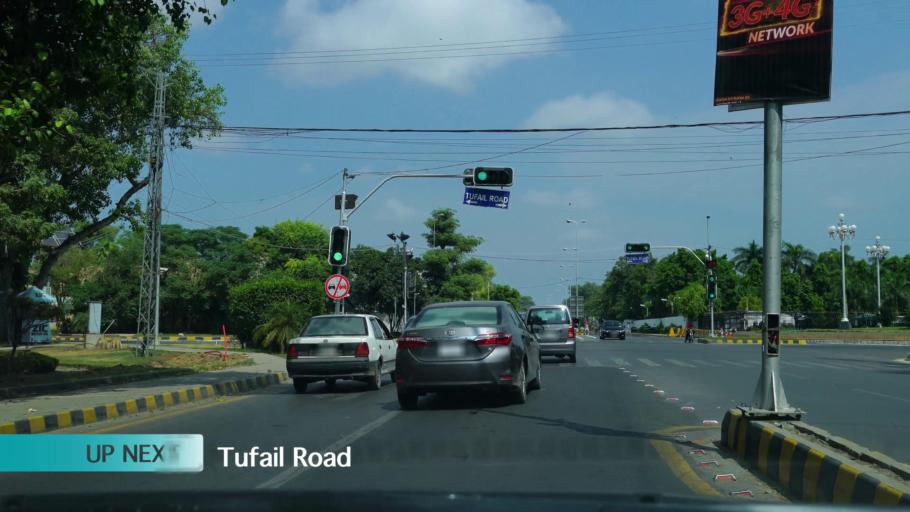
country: PK
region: Punjab
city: Lahore
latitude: 31.5265
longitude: 74.3800
